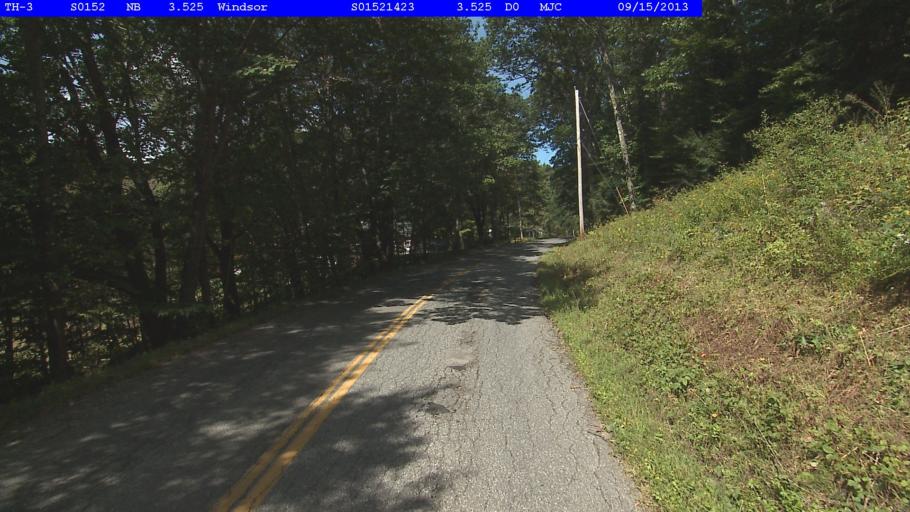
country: US
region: Vermont
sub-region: Windsor County
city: Windsor
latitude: 43.5115
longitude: -72.4344
